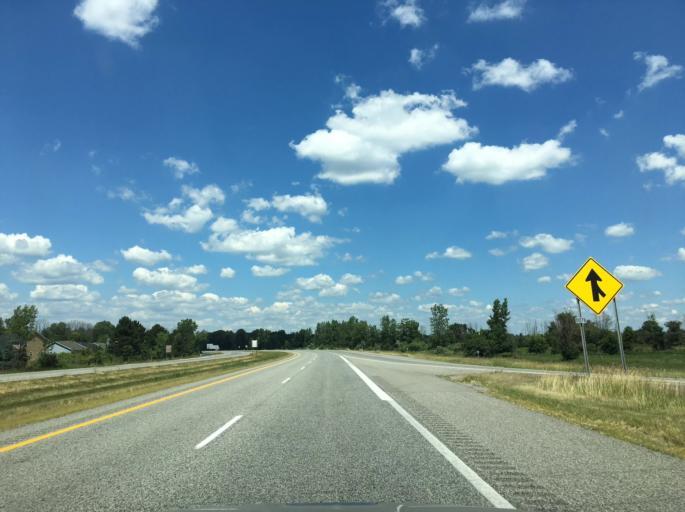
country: US
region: Michigan
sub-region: Midland County
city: Midland
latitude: 43.6431
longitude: -84.1891
